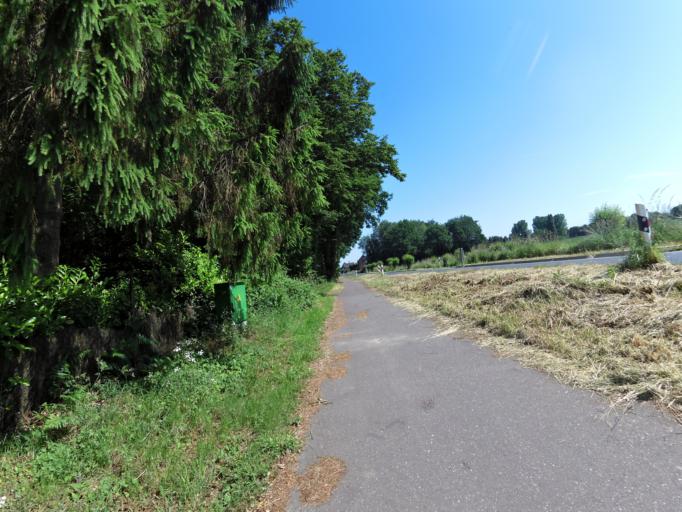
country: DE
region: North Rhine-Westphalia
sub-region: Regierungsbezirk Koln
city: Gangelt
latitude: 50.9784
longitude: 6.0250
